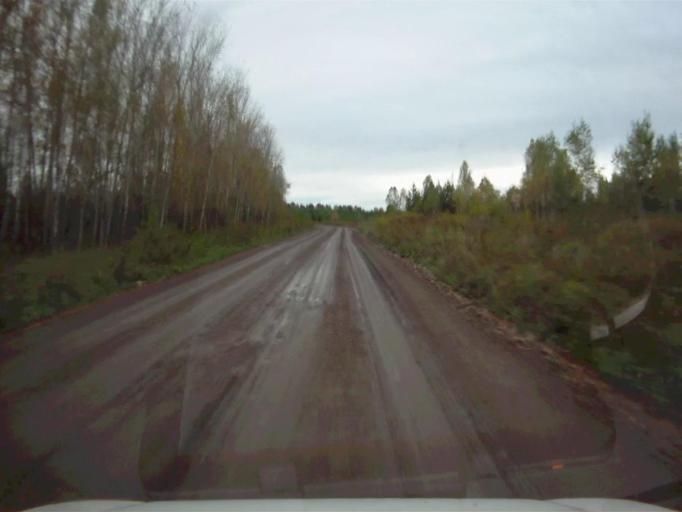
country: RU
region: Chelyabinsk
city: Nyazepetrovsk
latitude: 56.1372
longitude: 59.3007
